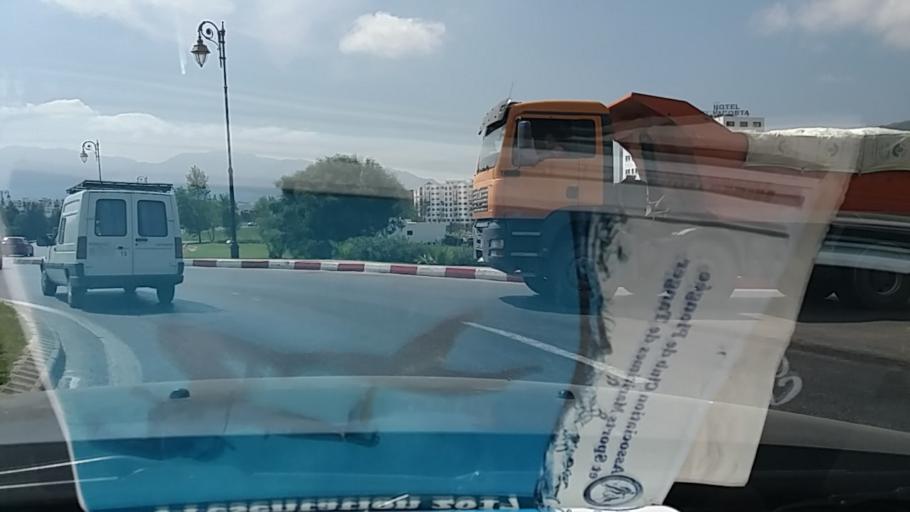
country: MA
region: Tanger-Tetouan
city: Tetouan
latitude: 35.6005
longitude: -5.3368
